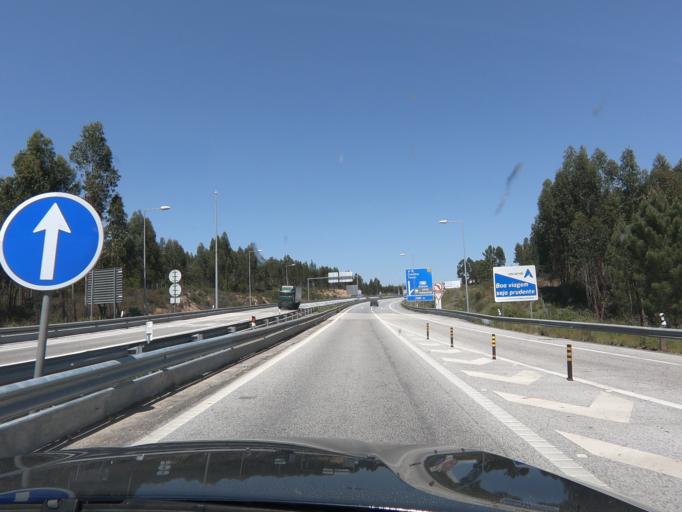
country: PT
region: Santarem
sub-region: Entroncamento
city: Entroncamento
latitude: 39.4903
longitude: -8.4467
